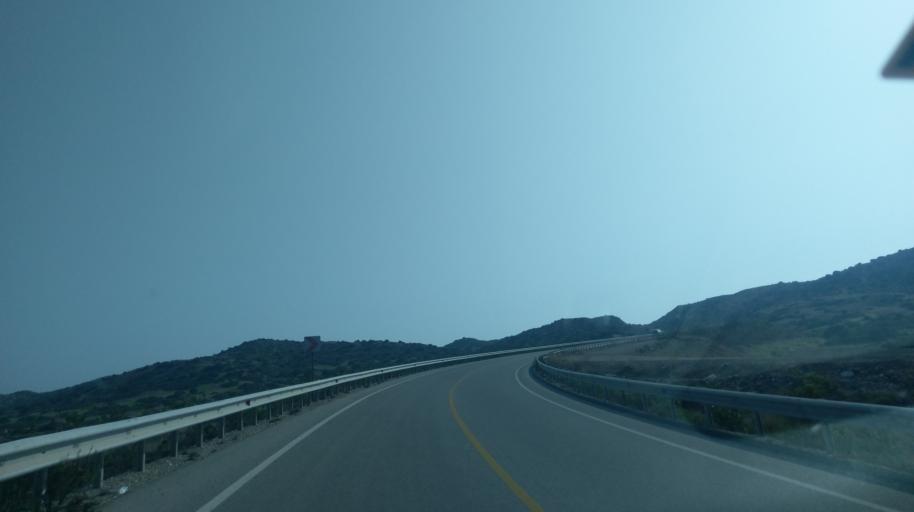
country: CY
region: Ammochostos
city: Leonarisso
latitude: 35.4936
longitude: 34.0968
